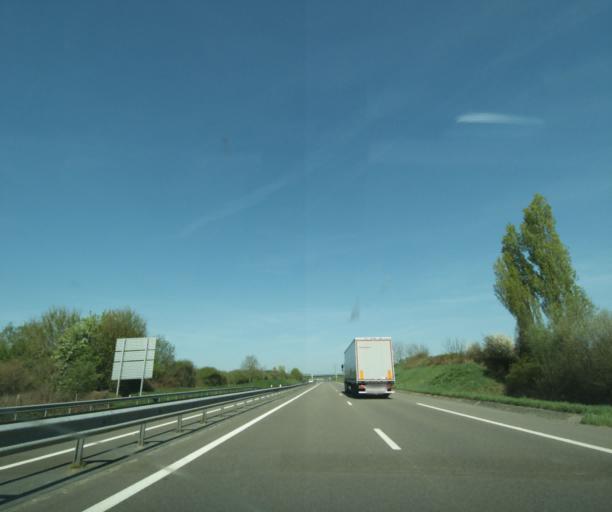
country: FR
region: Bourgogne
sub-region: Departement de la Nievre
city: Saint-Eloi
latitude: 46.9898
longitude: 3.2063
